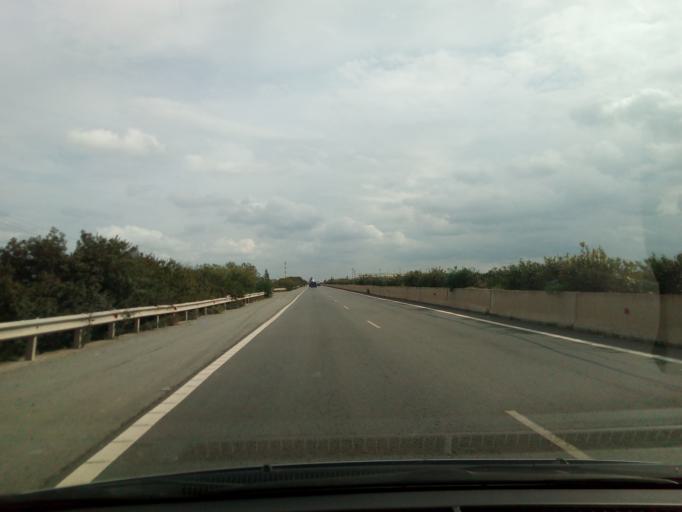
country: CY
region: Lefkosia
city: Kato Deftera
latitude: 35.1423
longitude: 33.2703
